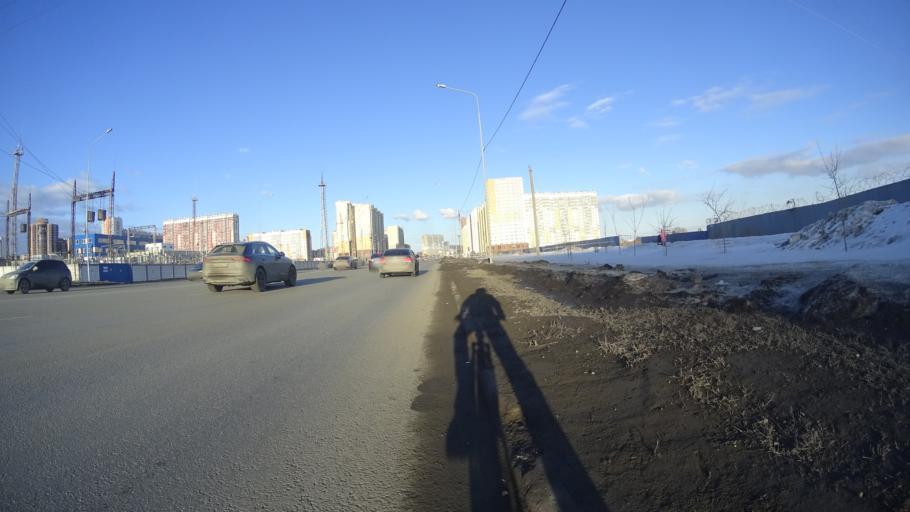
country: RU
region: Chelyabinsk
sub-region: Gorod Chelyabinsk
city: Chelyabinsk
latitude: 55.1684
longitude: 61.3051
